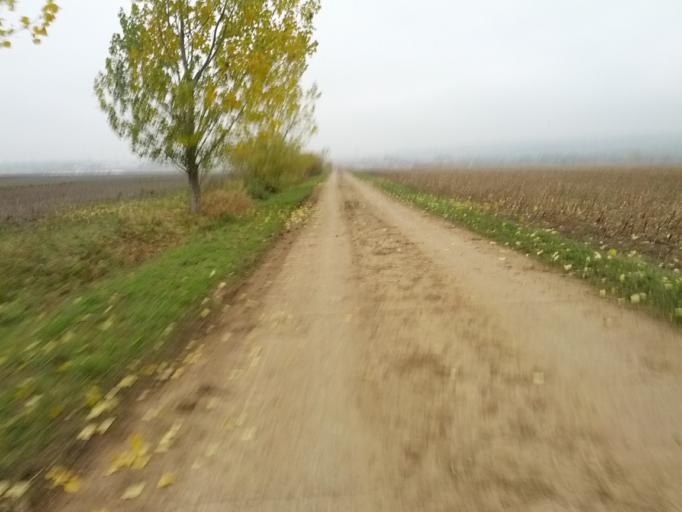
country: DE
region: Thuringia
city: Seebach
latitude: 50.9788
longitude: 10.4086
